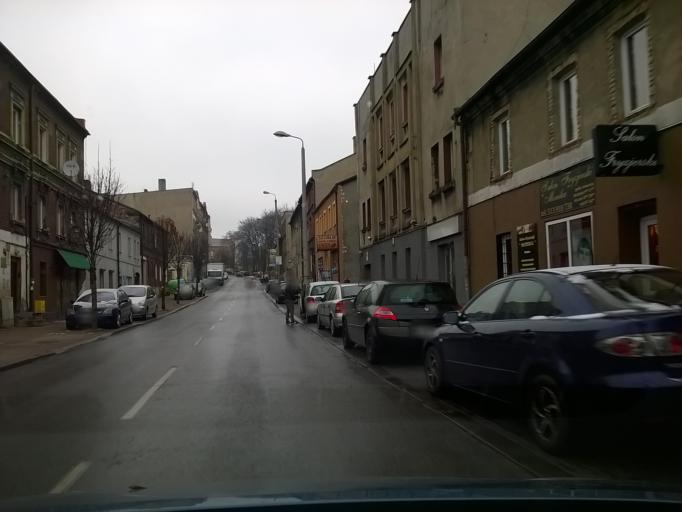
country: PL
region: Silesian Voivodeship
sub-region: Swietochlowice
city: Swietochlowice
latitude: 50.2951
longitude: 18.9404
